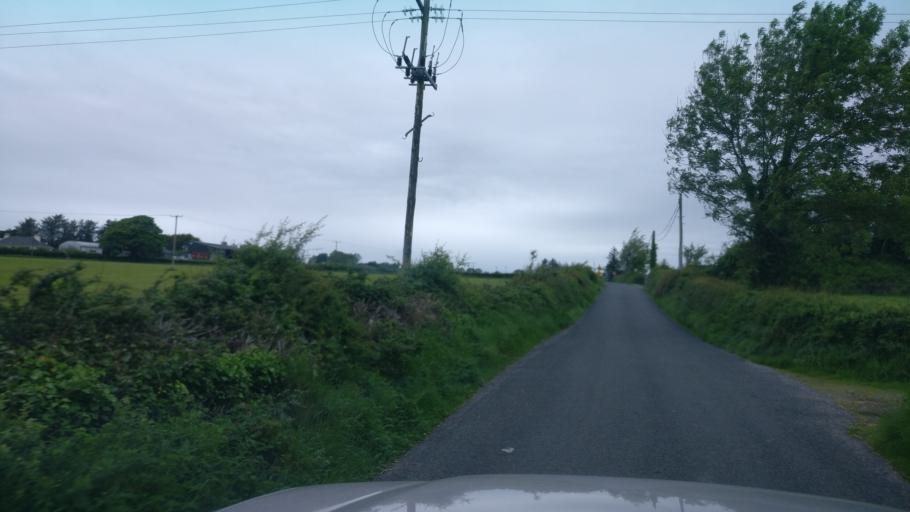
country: IE
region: Connaught
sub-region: County Galway
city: Loughrea
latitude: 53.1194
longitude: -8.4305
